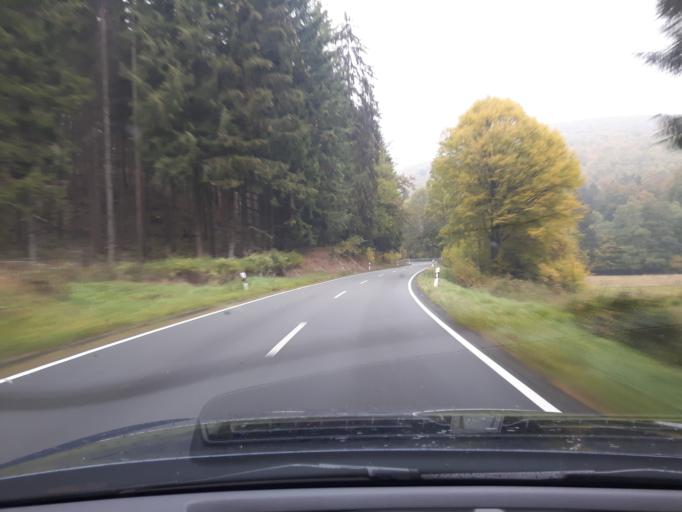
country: DE
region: North Rhine-Westphalia
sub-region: Regierungsbezirk Arnsberg
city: Bad Laasphe
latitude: 50.9564
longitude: 8.3929
